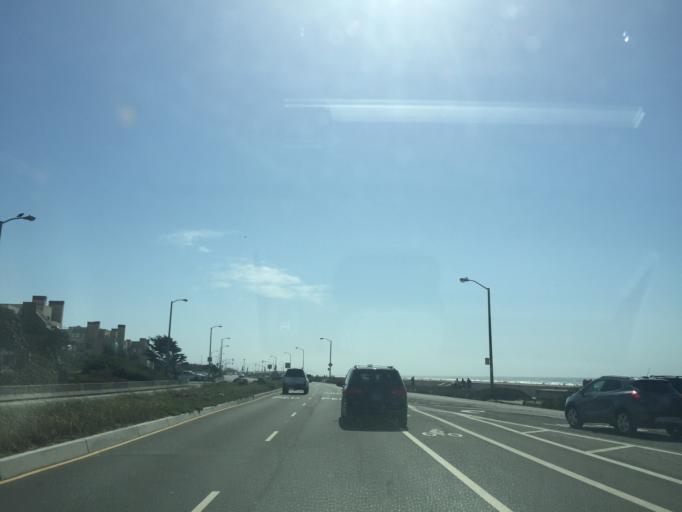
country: US
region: California
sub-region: San Mateo County
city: Daly City
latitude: 37.7739
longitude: -122.5113
